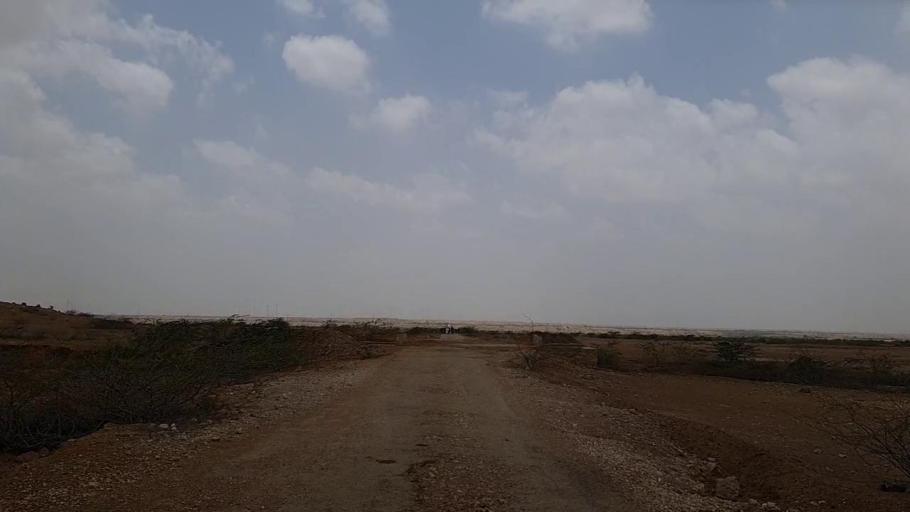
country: PK
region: Sindh
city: Thatta
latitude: 24.9008
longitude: 67.8979
